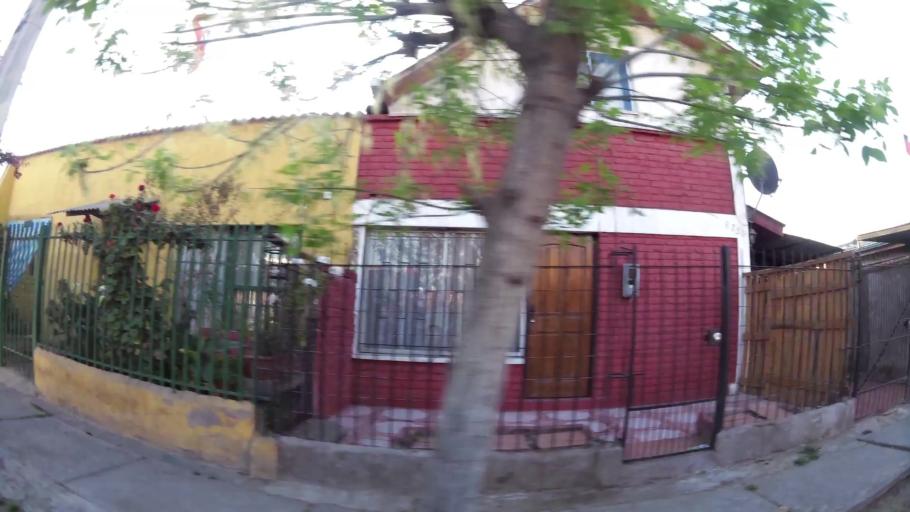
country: CL
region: Santiago Metropolitan
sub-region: Provincia de Santiago
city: La Pintana
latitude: -33.5205
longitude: -70.6220
